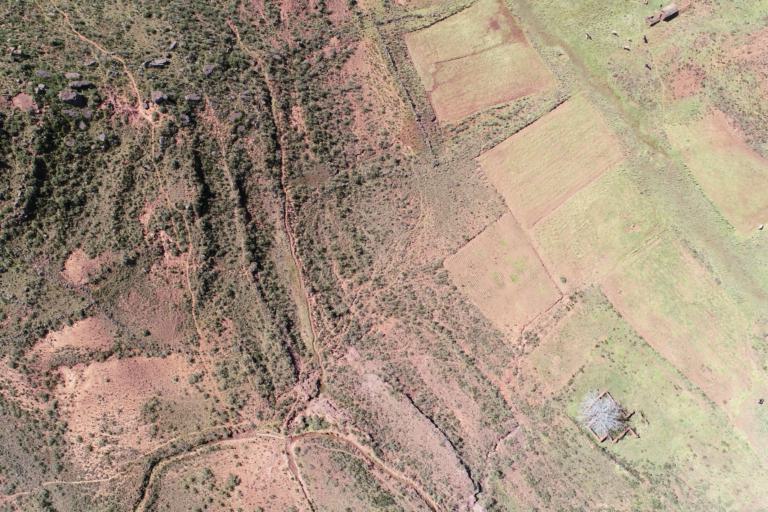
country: BO
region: La Paz
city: Tiahuanaco
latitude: -16.6067
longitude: -68.7756
